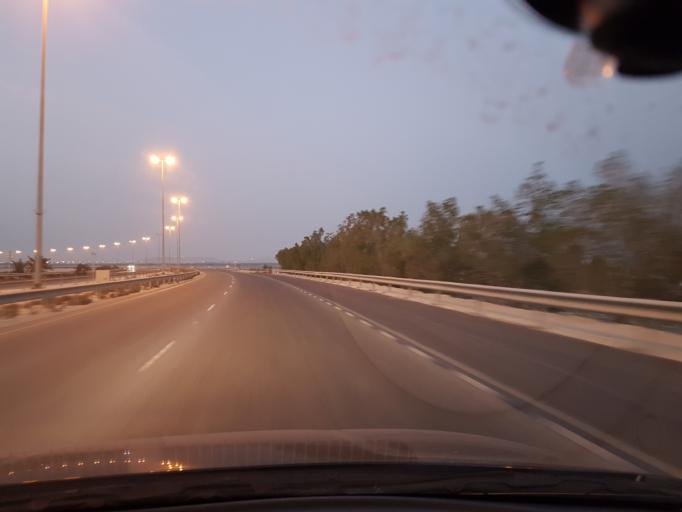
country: BH
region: Central Governorate
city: Dar Kulayb
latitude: 25.9934
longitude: 50.4806
